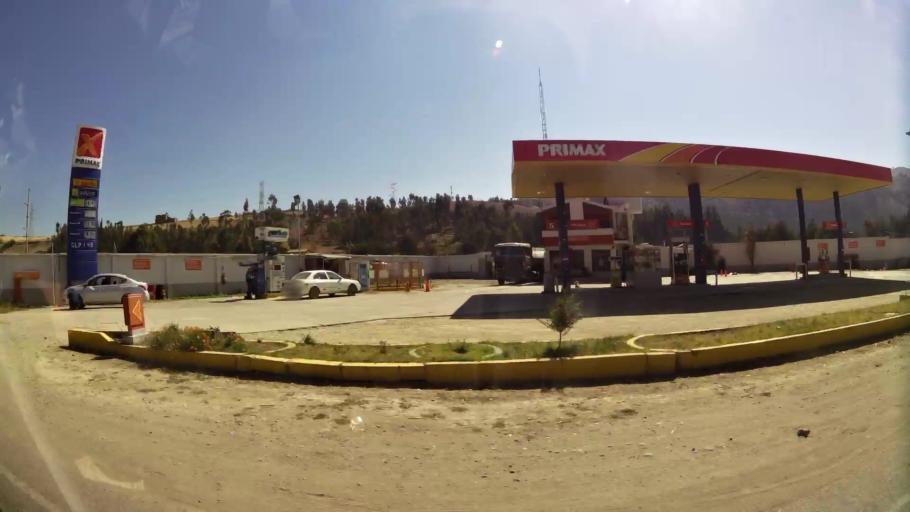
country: PE
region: Junin
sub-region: Provincia de Concepcion
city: Concepcion
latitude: -11.9385
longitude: -75.3082
